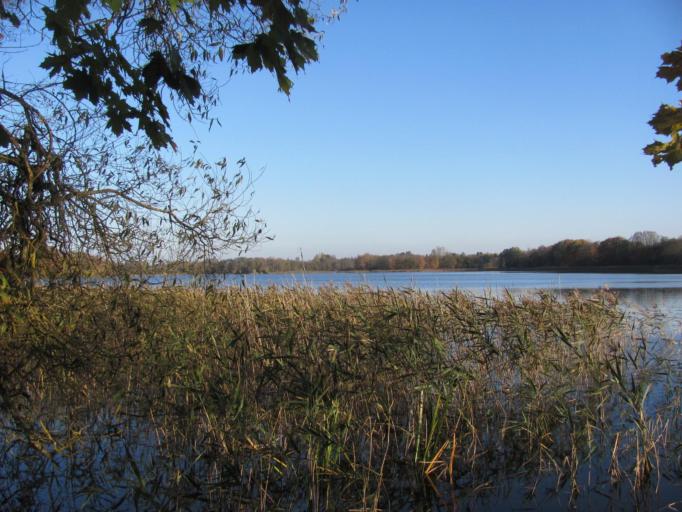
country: LT
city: Moletai
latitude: 55.4597
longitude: 25.3489
